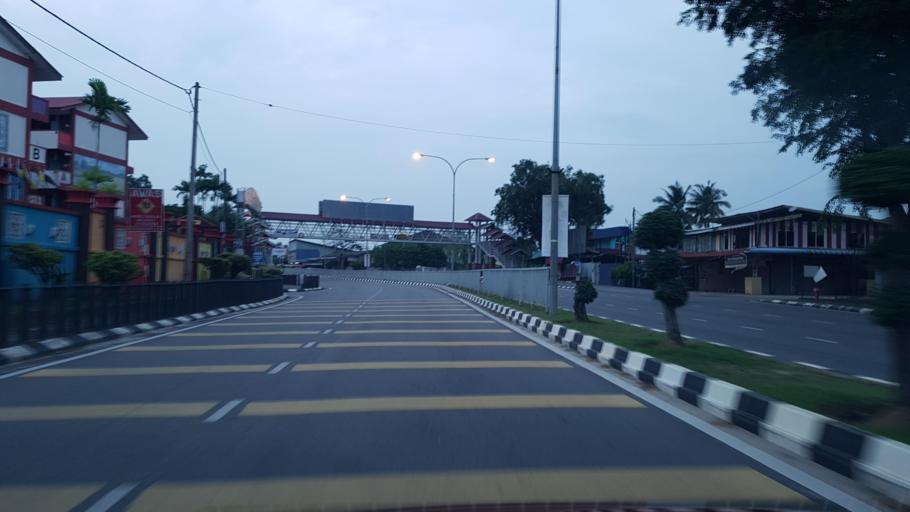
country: MY
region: Terengganu
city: Kuala Terengganu
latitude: 5.3156
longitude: 103.1447
